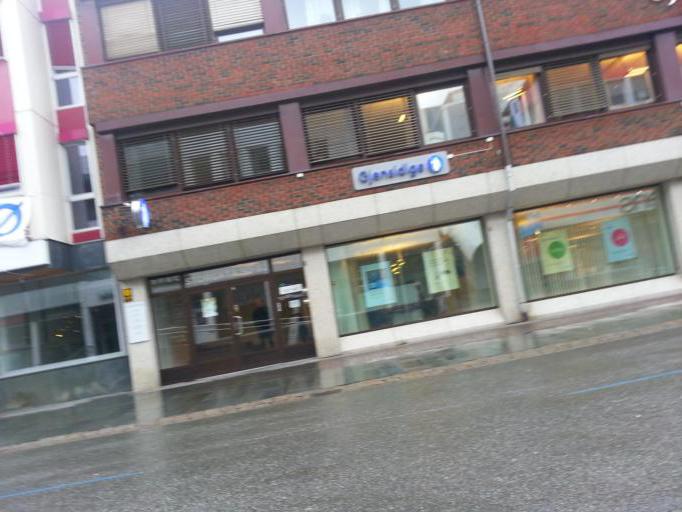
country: NO
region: Troms
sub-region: Tromso
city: Tromso
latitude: 69.6510
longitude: 18.9576
